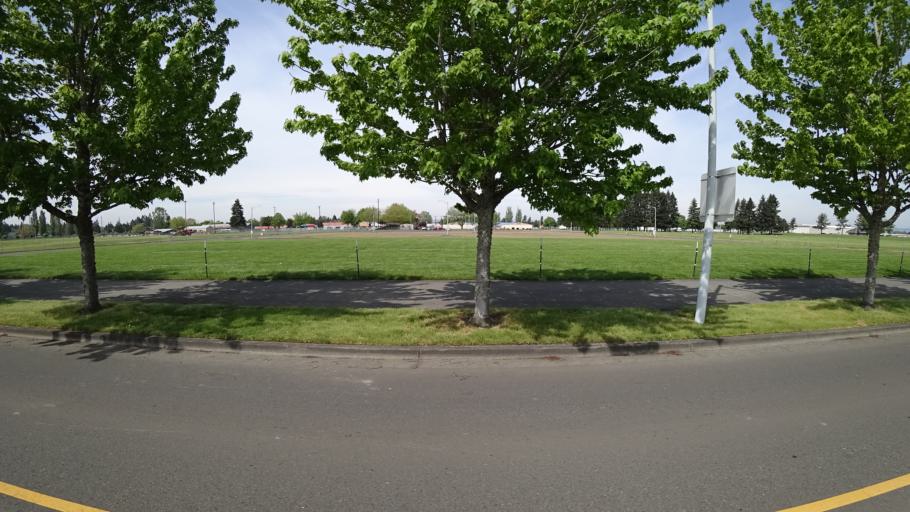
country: US
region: Oregon
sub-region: Washington County
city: Hillsboro
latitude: 45.5302
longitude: -122.9466
